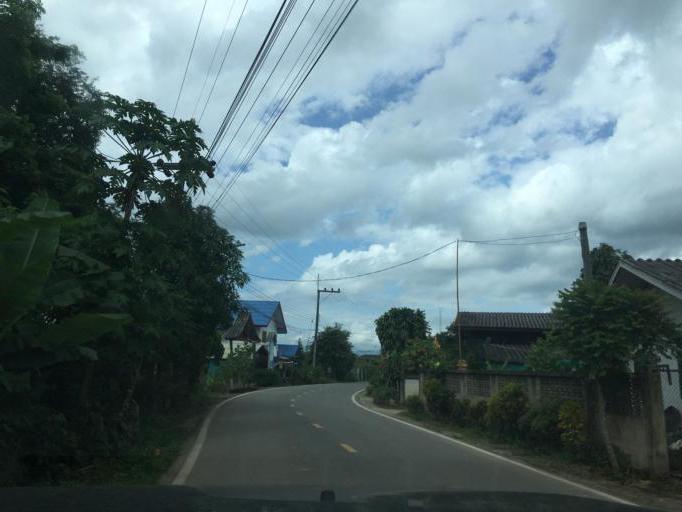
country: TH
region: Chiang Rai
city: Wiang Pa Pao
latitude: 19.2326
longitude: 99.5127
